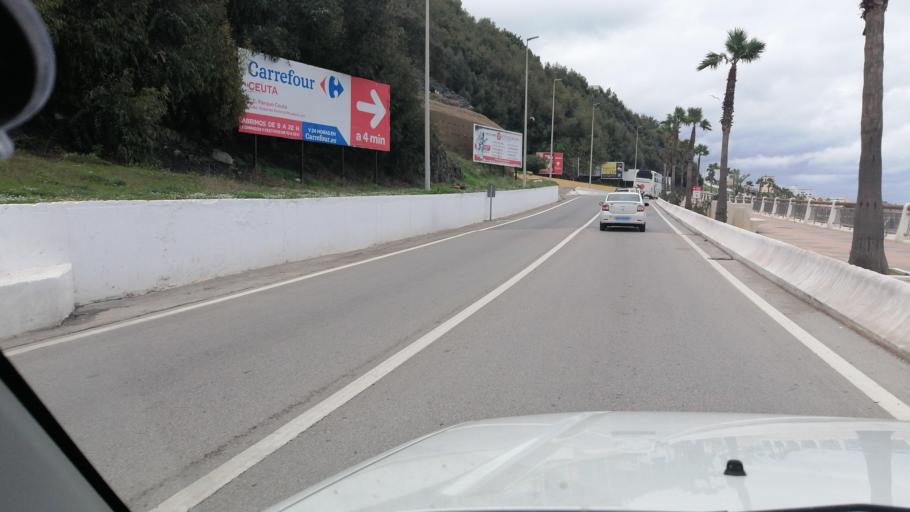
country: ES
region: Ceuta
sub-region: Ceuta
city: Ceuta
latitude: 35.8823
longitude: -5.3249
